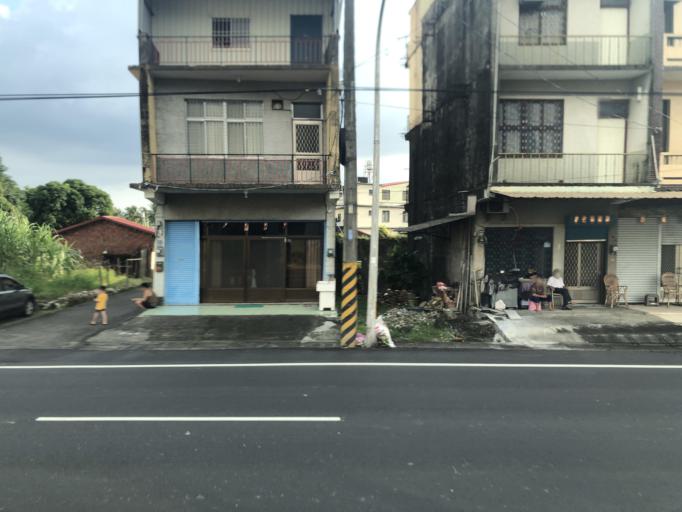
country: TW
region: Taiwan
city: Yujing
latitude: 22.9023
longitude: 120.5347
